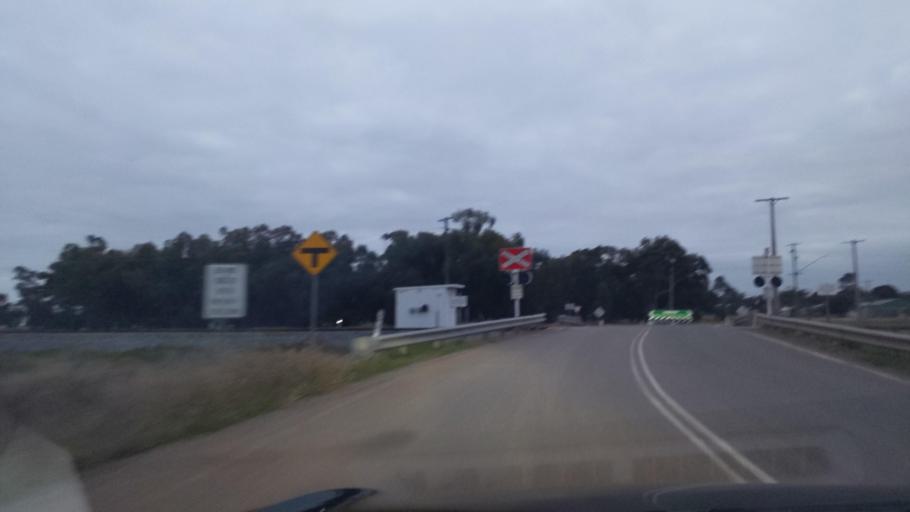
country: AU
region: New South Wales
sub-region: Narrandera
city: Narrandera
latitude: -34.7391
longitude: 146.7804
